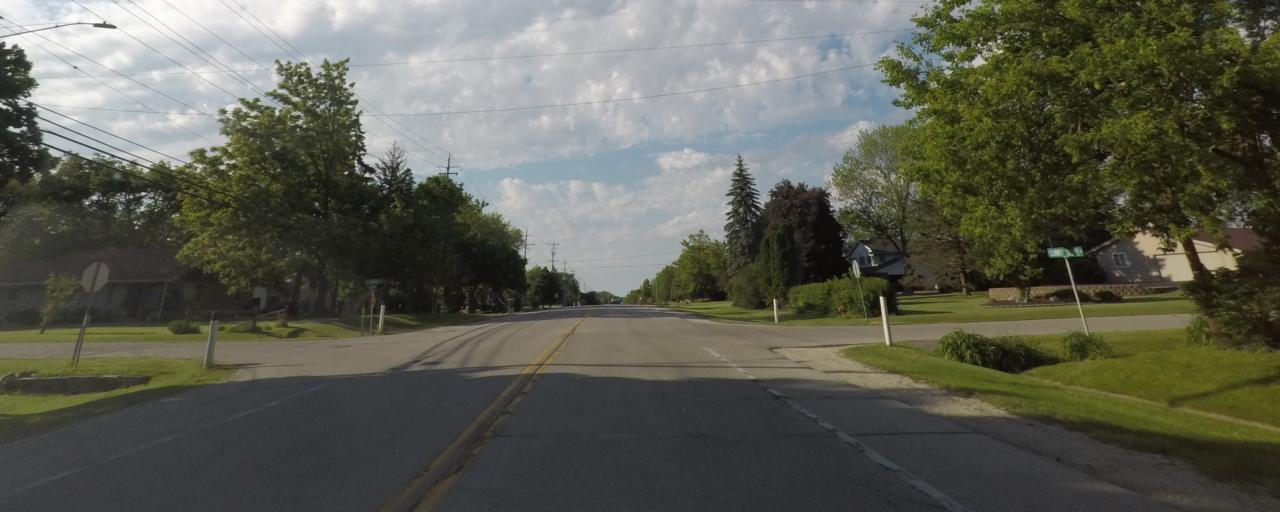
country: US
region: Wisconsin
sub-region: Waukesha County
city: New Berlin
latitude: 42.9486
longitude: -88.0893
